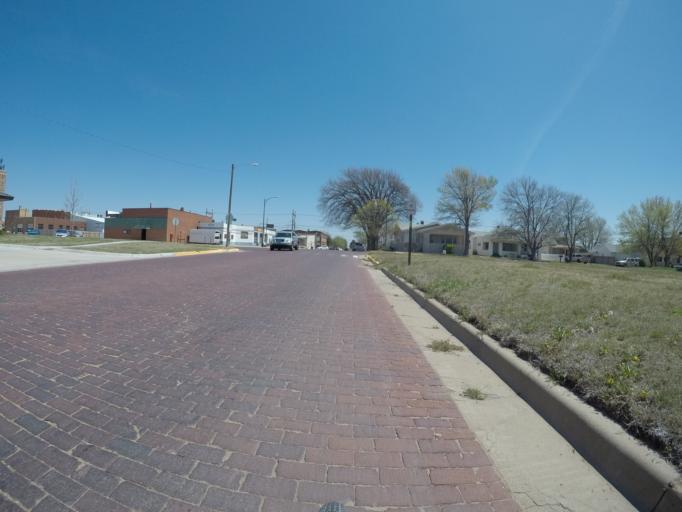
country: US
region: Kansas
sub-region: Pratt County
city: Pratt
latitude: 37.6418
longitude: -98.7412
